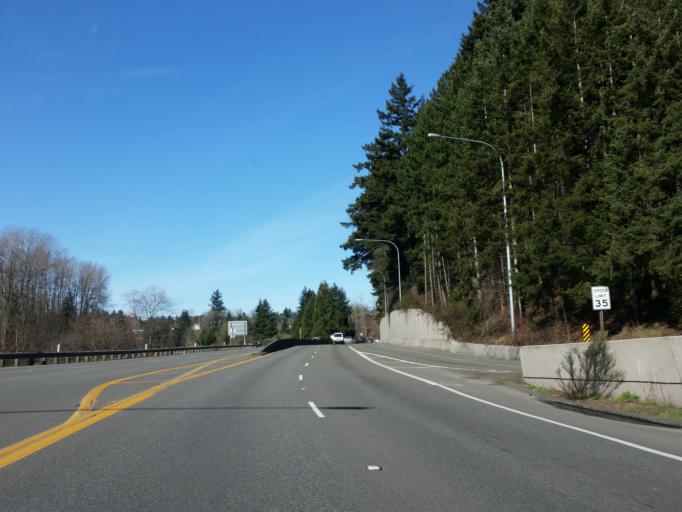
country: US
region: Washington
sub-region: King County
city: Bothell
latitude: 47.7558
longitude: -122.1957
